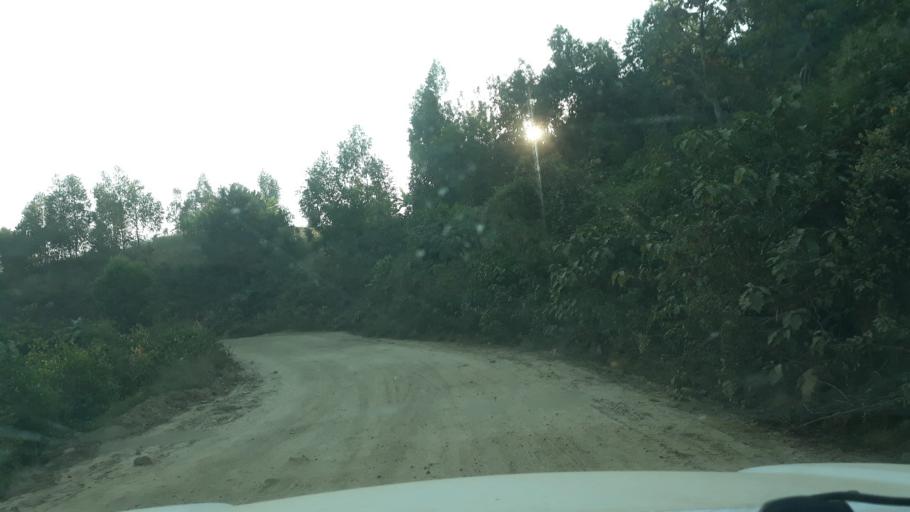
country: RW
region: Western Province
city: Cyangugu
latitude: -2.7027
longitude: 28.9404
